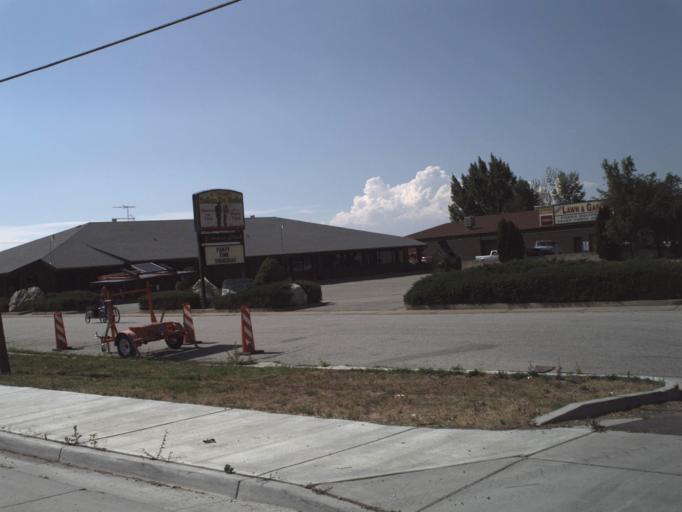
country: US
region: Utah
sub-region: Weber County
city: Ogden
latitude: 41.2444
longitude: -111.9841
